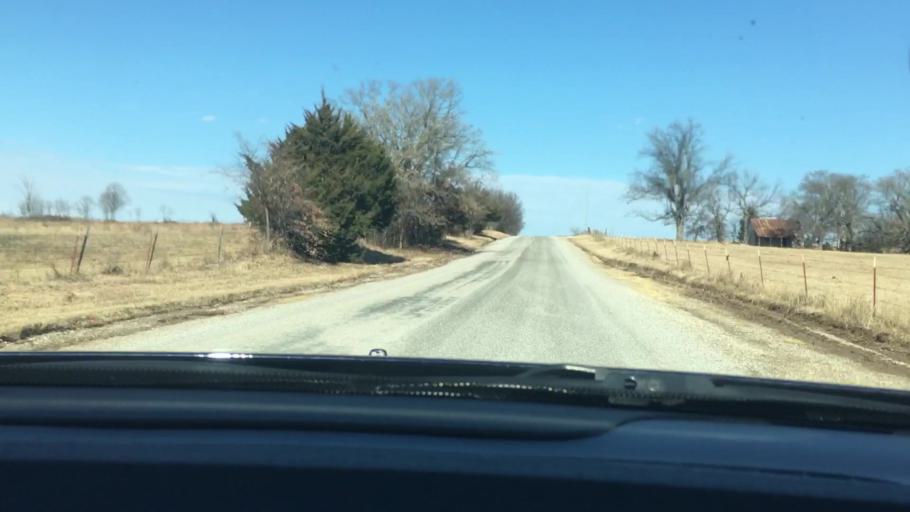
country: US
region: Oklahoma
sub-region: Garvin County
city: Wynnewood
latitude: 34.6536
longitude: -97.0902
